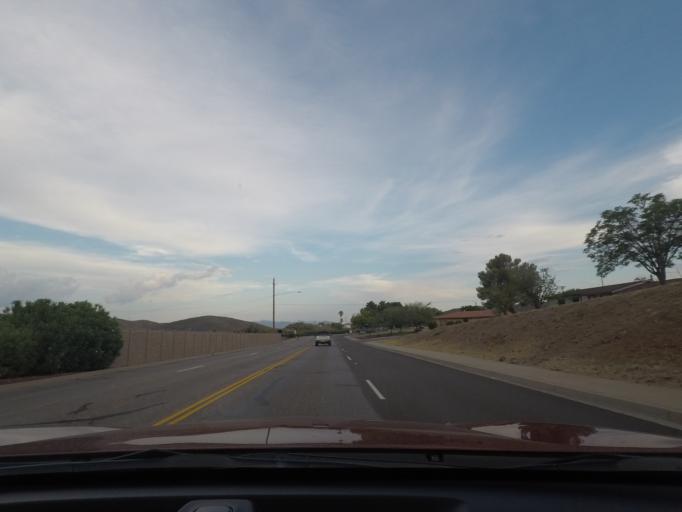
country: US
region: Arizona
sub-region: Yavapai County
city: Bagdad
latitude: 34.5710
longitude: -113.1772
